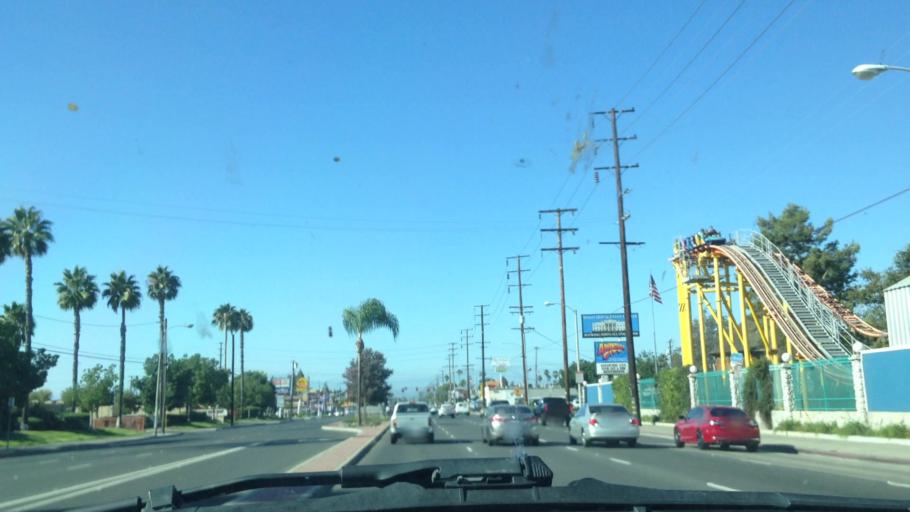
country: US
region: California
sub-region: Orange County
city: Stanton
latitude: 33.8148
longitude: -117.9932
